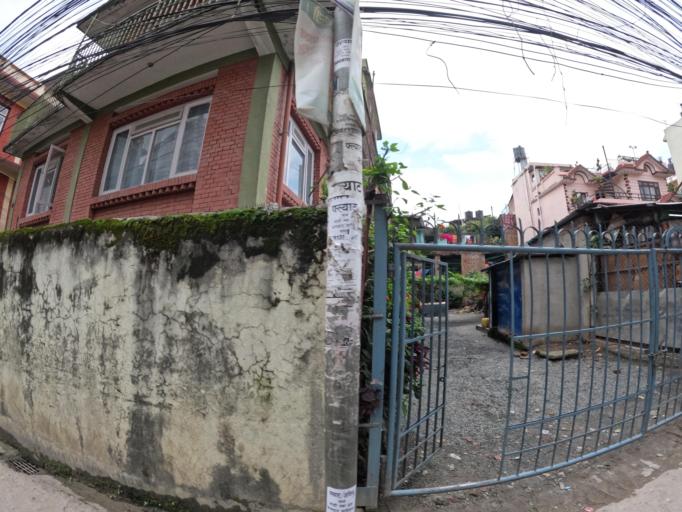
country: NP
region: Central Region
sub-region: Bagmati Zone
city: Kathmandu
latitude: 27.7390
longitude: 85.3144
